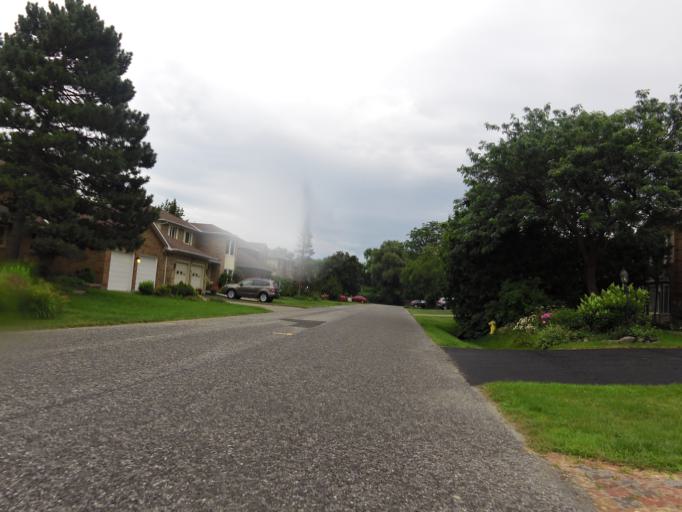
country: CA
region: Ontario
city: Bells Corners
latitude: 45.3538
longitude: -75.8457
